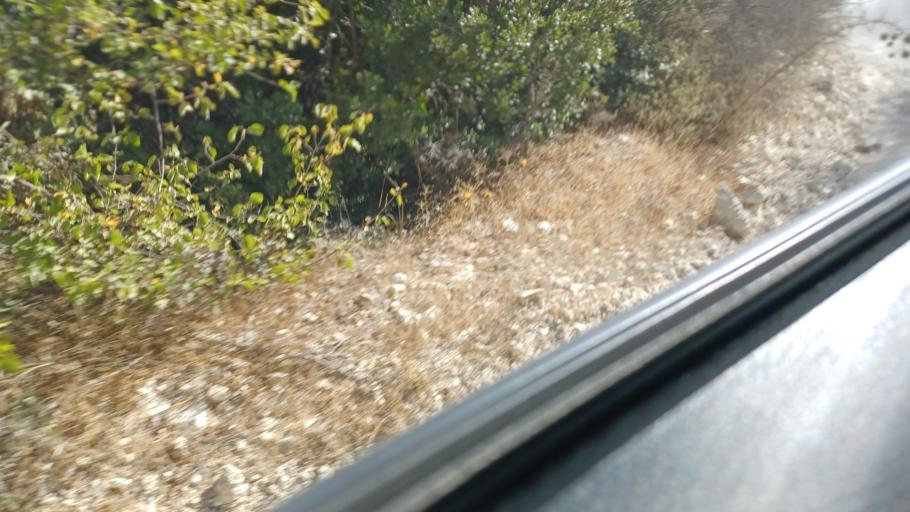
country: CY
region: Pafos
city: Tala
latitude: 34.8653
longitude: 32.4413
